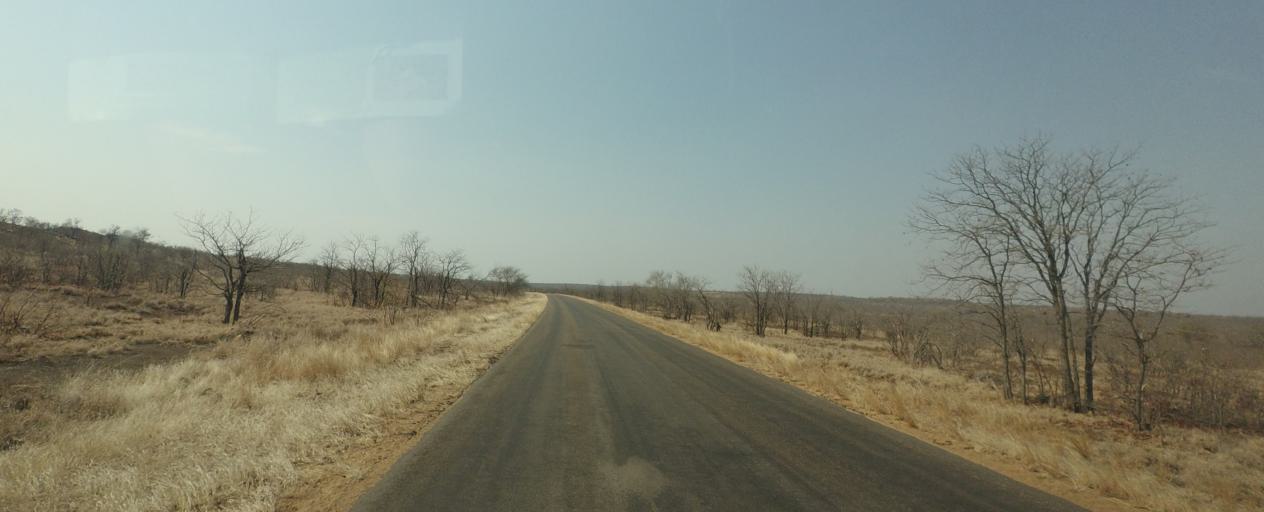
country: ZA
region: Limpopo
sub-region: Mopani District Municipality
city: Phalaborwa
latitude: -23.9870
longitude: 31.6425
